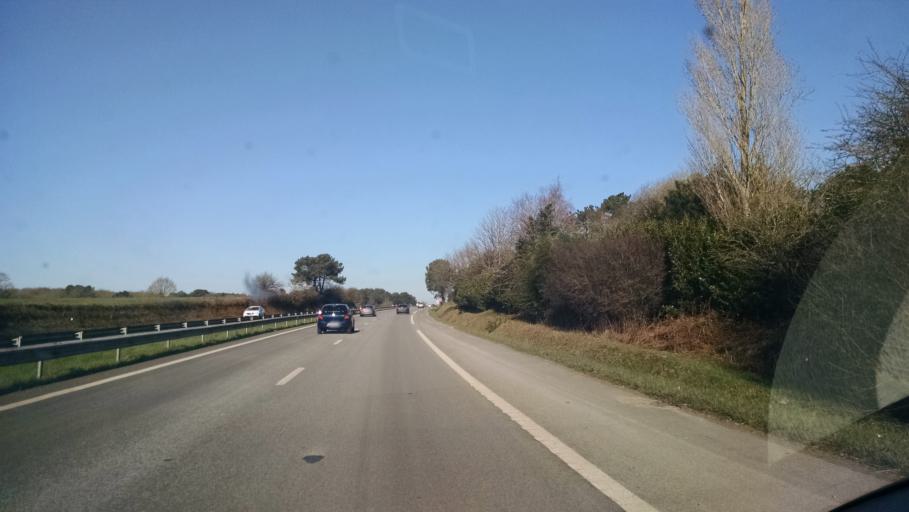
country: FR
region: Brittany
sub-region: Departement du Morbihan
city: Landaul
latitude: 47.7302
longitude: -3.0895
